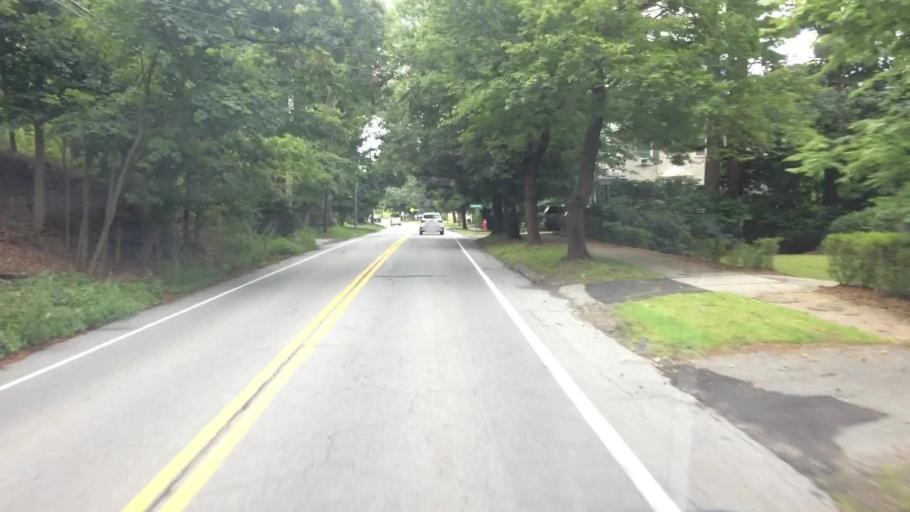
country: US
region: Massachusetts
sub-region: Middlesex County
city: Winchester
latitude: 42.4574
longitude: -71.1272
